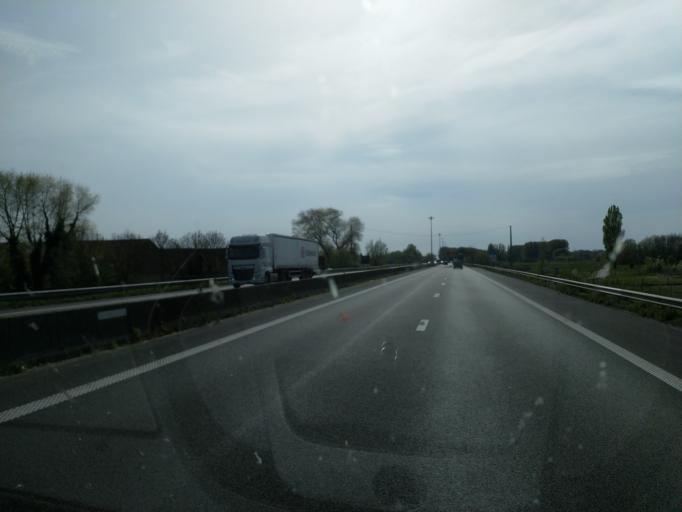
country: FR
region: Nord-Pas-de-Calais
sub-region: Departement du Nord
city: Ghyvelde
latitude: 51.0578
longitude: 2.5638
